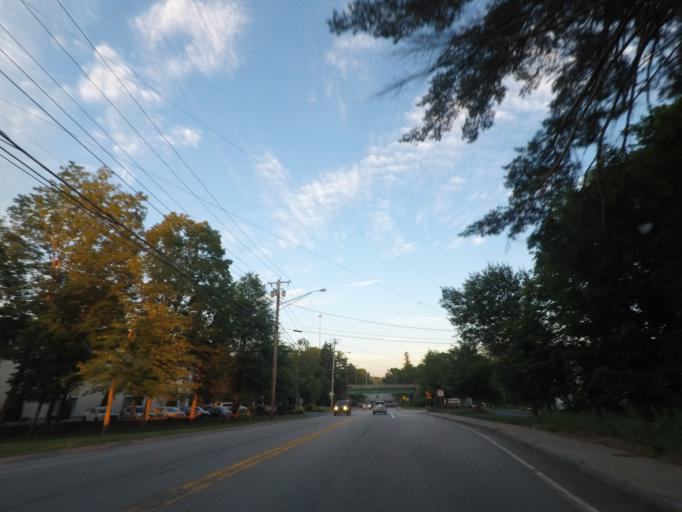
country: US
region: Massachusetts
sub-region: Worcester County
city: Sturbridge
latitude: 42.1107
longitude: -72.0839
